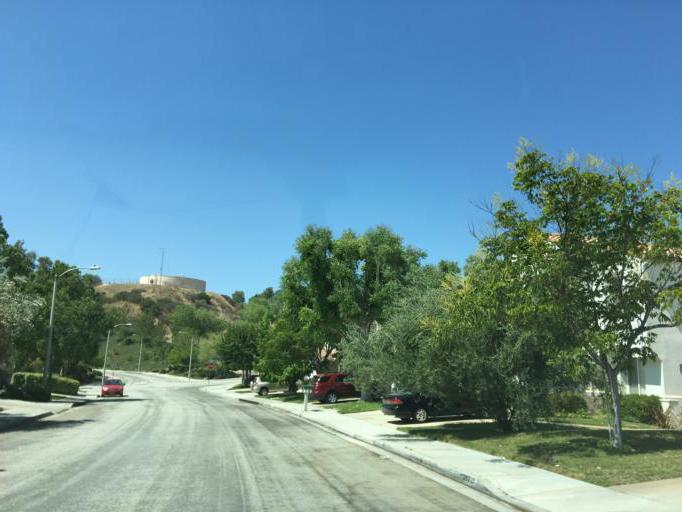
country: US
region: California
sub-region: Los Angeles County
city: Santa Clarita
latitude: 34.3938
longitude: -118.5902
